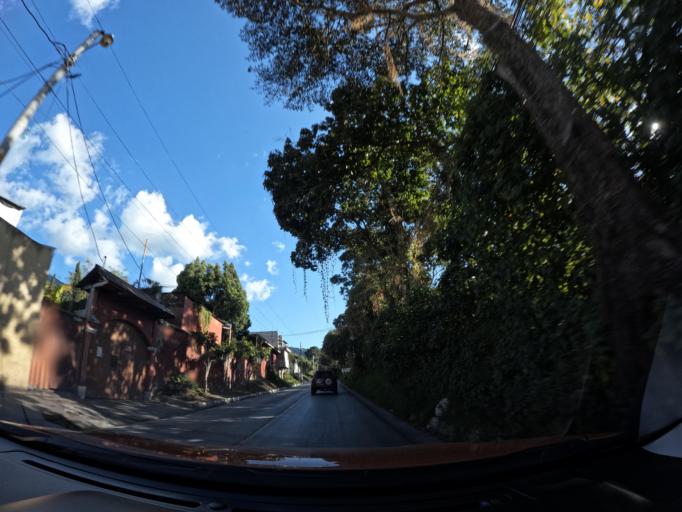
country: GT
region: Sacatepequez
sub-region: Municipio de Santa Maria de Jesus
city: Santa Maria de Jesus
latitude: 14.5302
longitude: -90.7274
